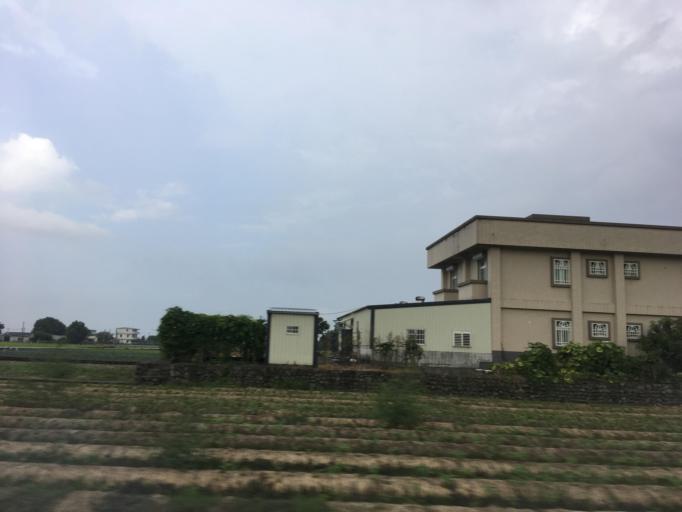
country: TW
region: Taiwan
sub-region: Yilan
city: Yilan
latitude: 24.6682
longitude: 121.6354
